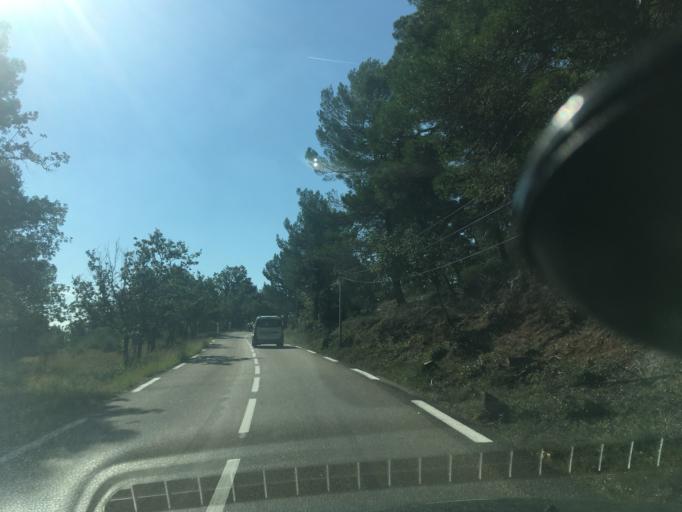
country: FR
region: Provence-Alpes-Cote d'Azur
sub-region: Departement du Var
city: Regusse
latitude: 43.6149
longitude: 6.0692
